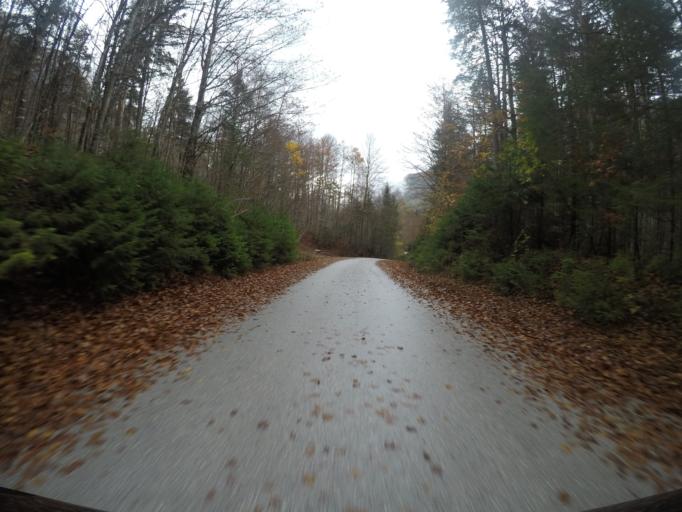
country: SI
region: Kranjska Gora
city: Mojstrana
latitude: 46.4165
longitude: 13.8521
